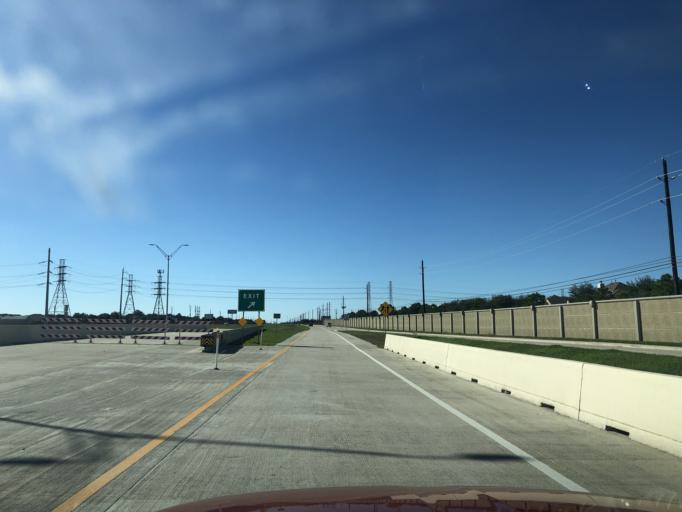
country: US
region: Texas
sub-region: Fort Bend County
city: Cinco Ranch
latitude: 29.6971
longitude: -95.8185
